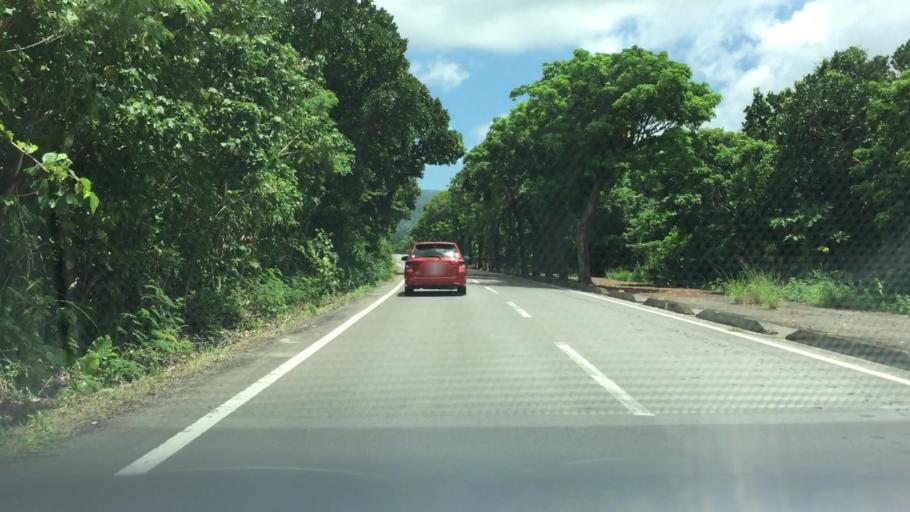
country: JP
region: Okinawa
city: Ishigaki
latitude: 24.3889
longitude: 124.1404
